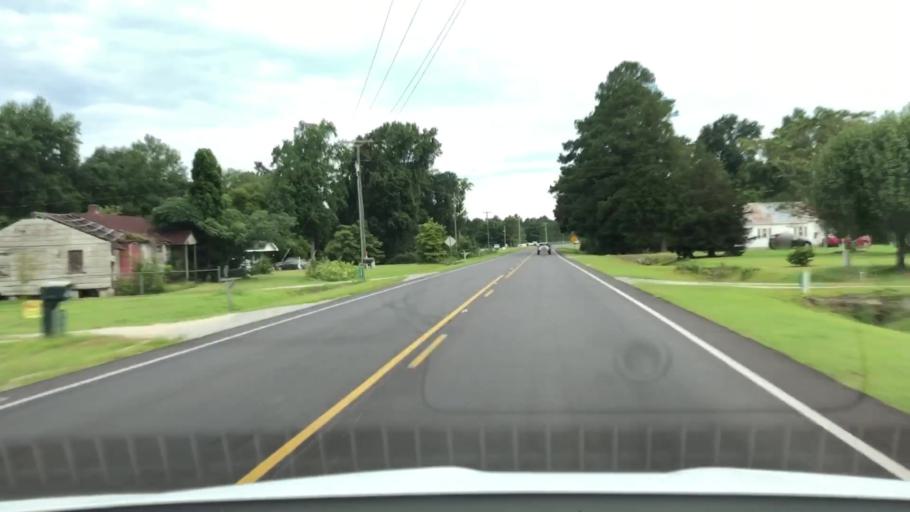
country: US
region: North Carolina
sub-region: Jones County
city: Maysville
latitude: 34.8810
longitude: -77.2071
